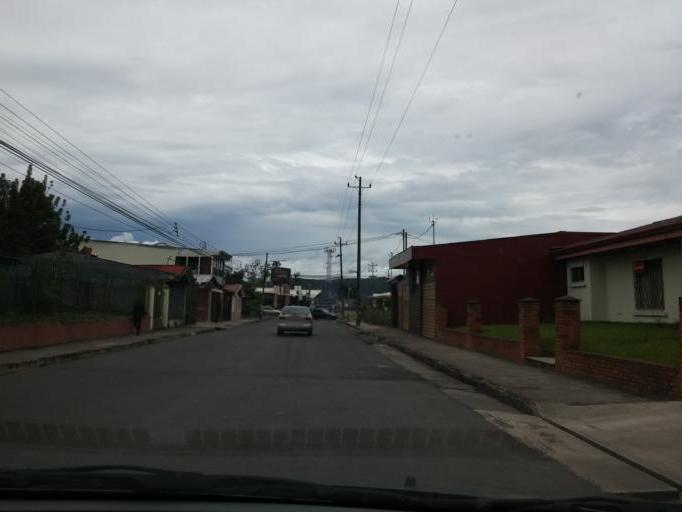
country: CR
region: Cartago
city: Cartago
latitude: 9.8597
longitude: -83.9172
